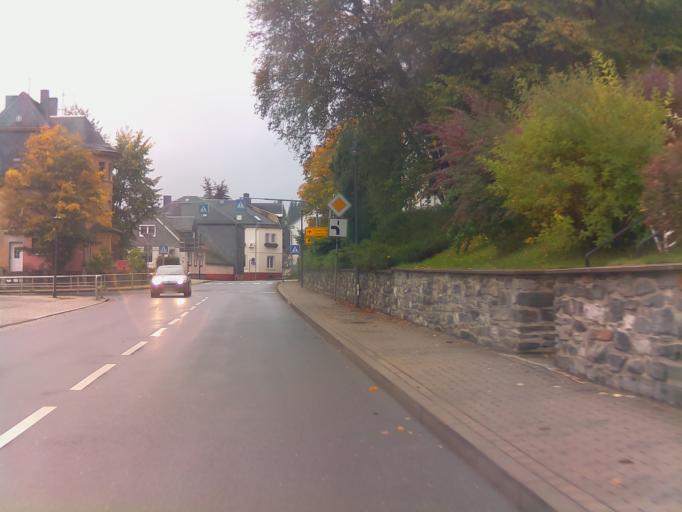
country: DE
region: Thuringia
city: Wurzbach
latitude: 50.4643
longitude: 11.5389
